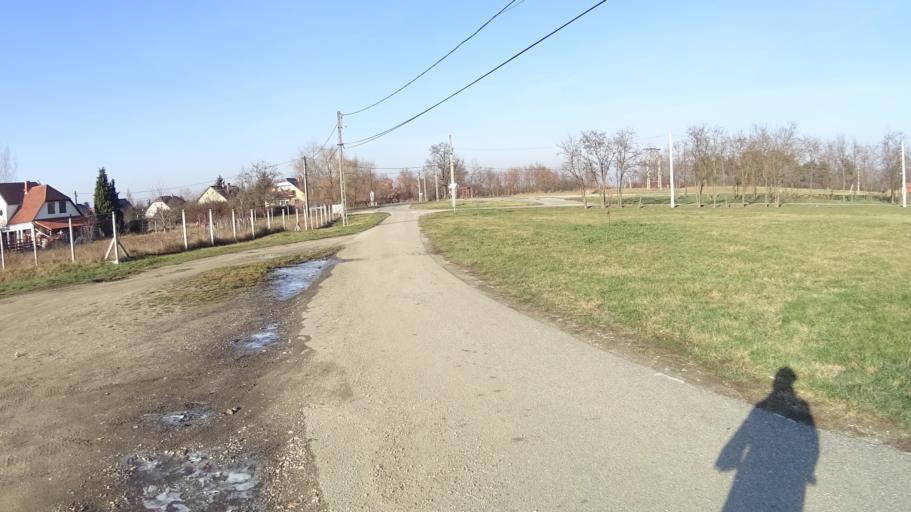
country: HU
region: Borsod-Abauj-Zemplen
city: Nyekladhaza
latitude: 47.9928
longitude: 20.8582
